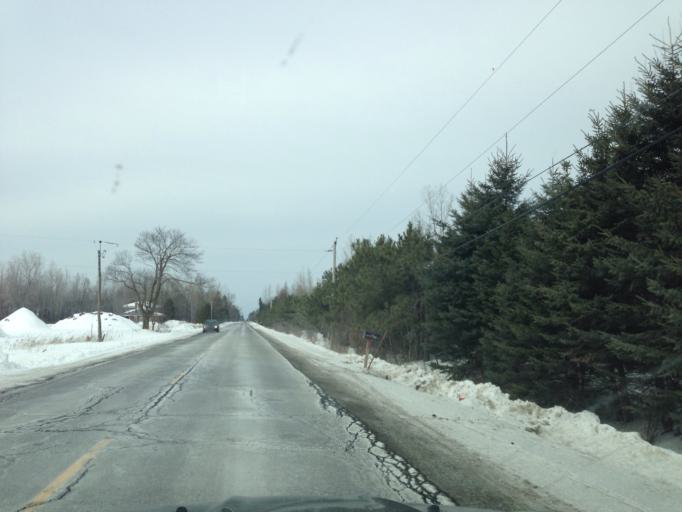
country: CA
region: Ontario
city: Ottawa
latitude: 45.3239
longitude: -75.5411
